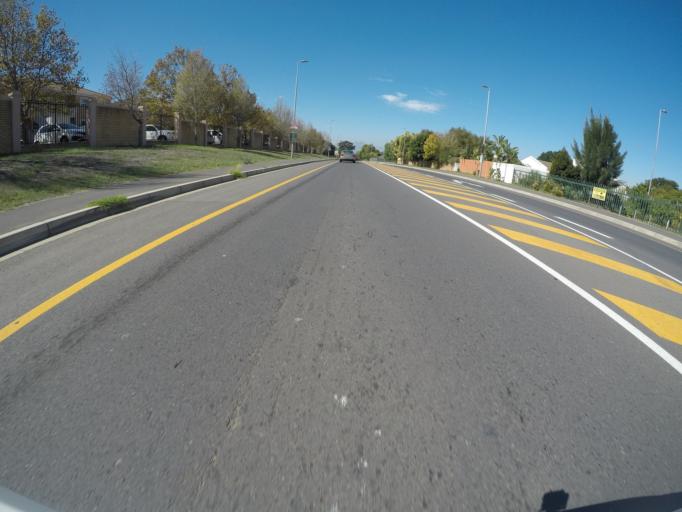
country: ZA
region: Western Cape
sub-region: City of Cape Town
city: Kraaifontein
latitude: -33.8296
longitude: 18.6408
